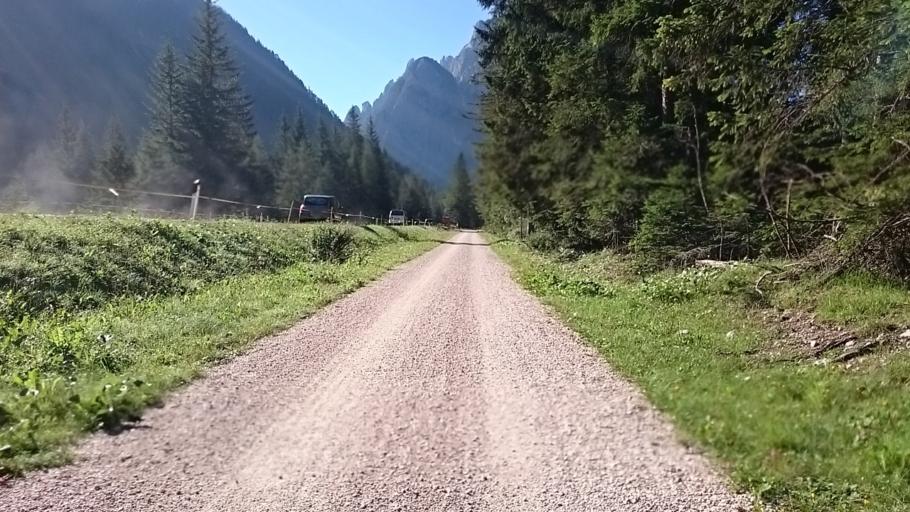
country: IT
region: Trentino-Alto Adige
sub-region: Bolzano
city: Dobbiaco
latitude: 46.6485
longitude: 12.2305
